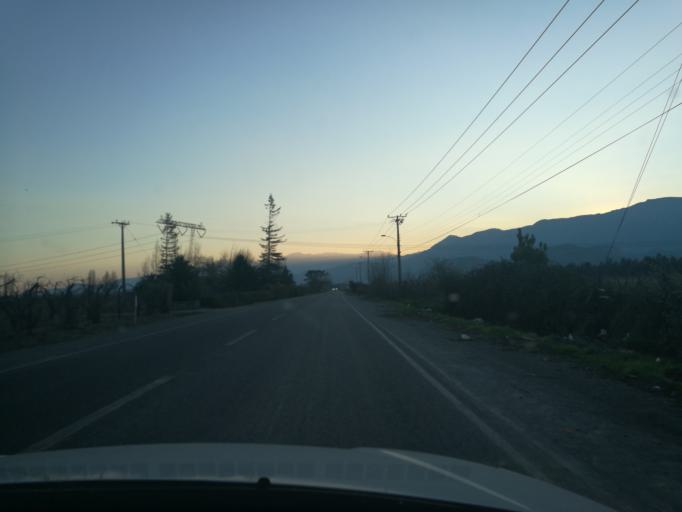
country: CL
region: O'Higgins
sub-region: Provincia de Cachapoal
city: Graneros
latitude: -34.0347
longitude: -70.6751
